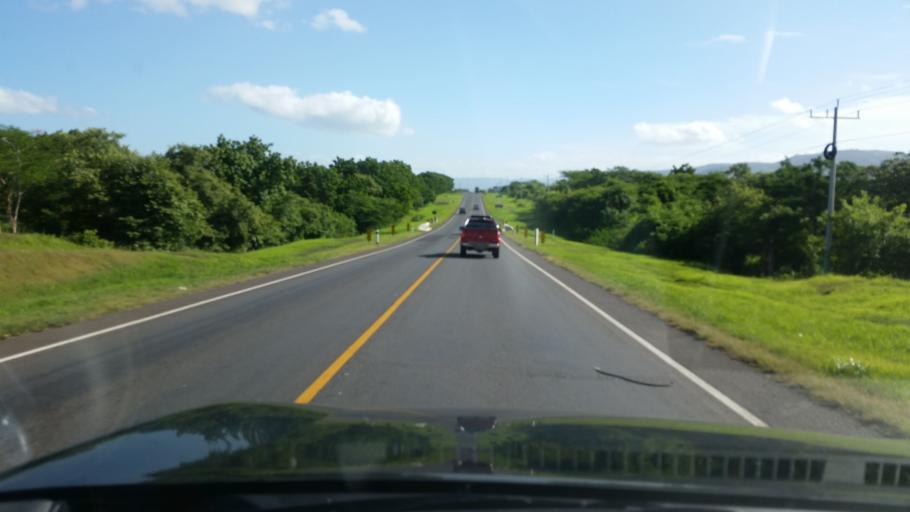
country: NI
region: Managua
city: Tipitapa
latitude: 12.3633
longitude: -86.0478
